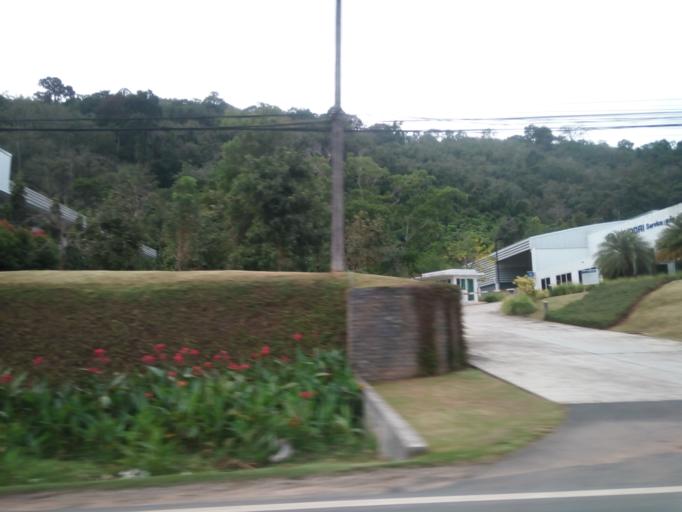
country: TH
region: Phuket
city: Wichit
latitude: 7.9166
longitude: 98.3691
